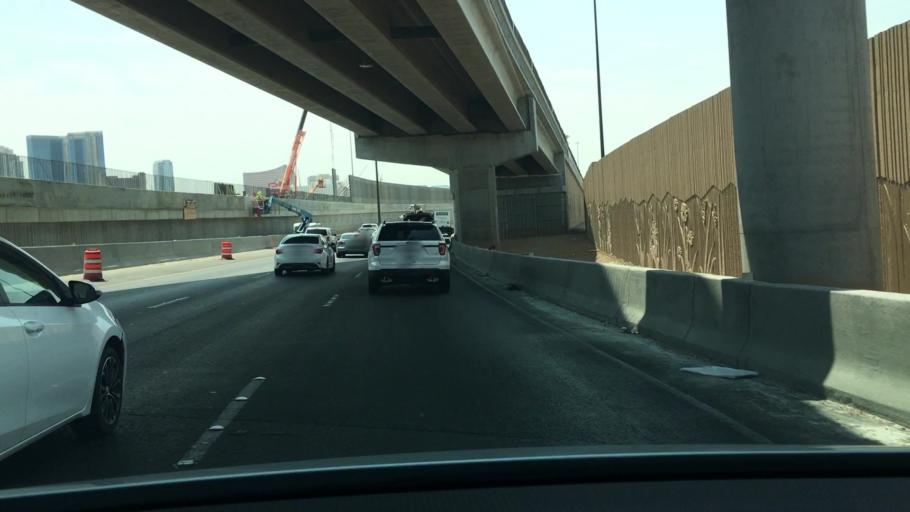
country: US
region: Nevada
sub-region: Clark County
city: Las Vegas
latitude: 36.1566
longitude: -115.1618
